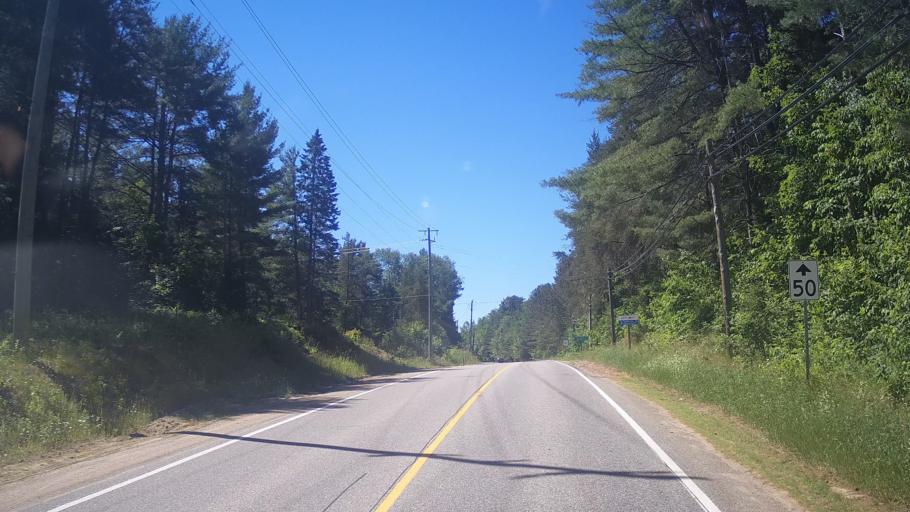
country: CA
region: Ontario
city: Huntsville
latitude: 45.3643
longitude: -79.2049
